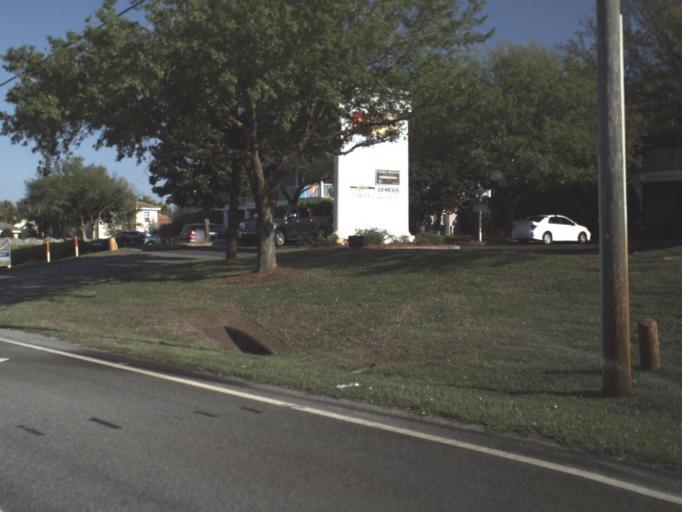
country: US
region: Florida
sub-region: Walton County
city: Miramar Beach
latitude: 30.3860
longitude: -86.4011
